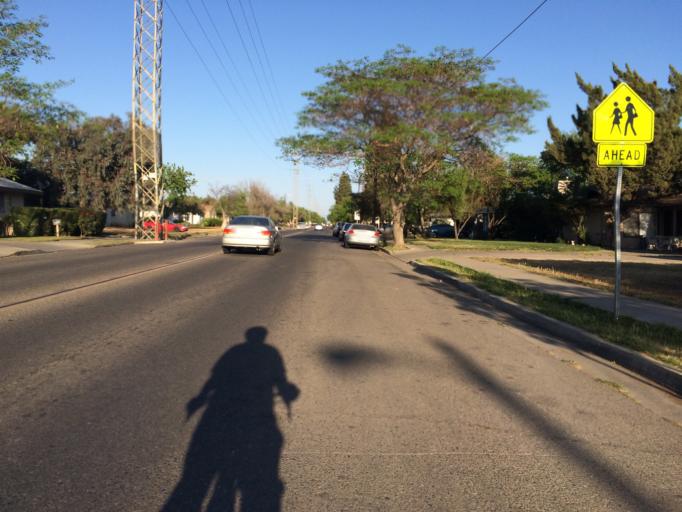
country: US
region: California
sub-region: Fresno County
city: Fresno
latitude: 36.7867
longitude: -119.7985
